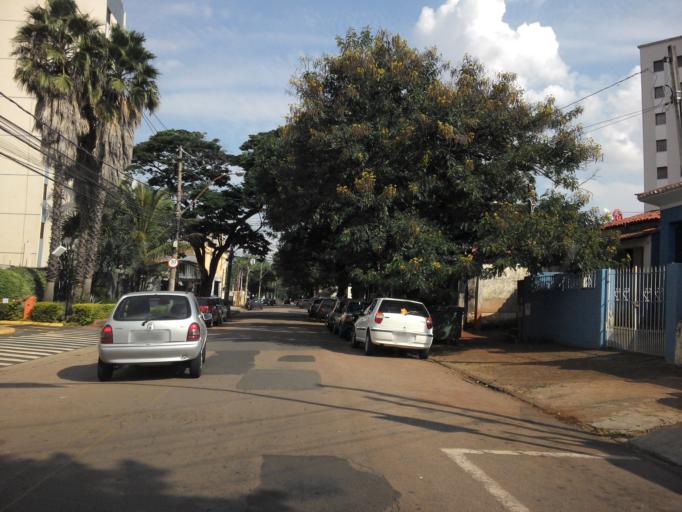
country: BR
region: Sao Paulo
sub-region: Campinas
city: Campinas
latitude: -22.8836
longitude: -47.0682
